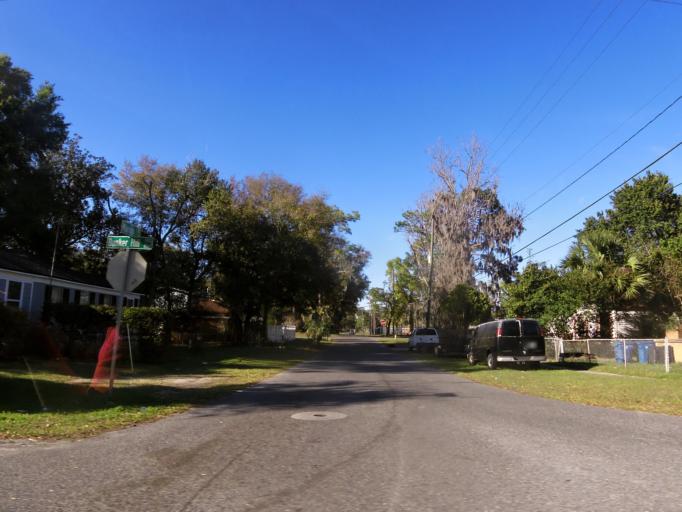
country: US
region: Florida
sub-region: Duval County
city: Jacksonville
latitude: 30.3952
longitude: -81.6718
